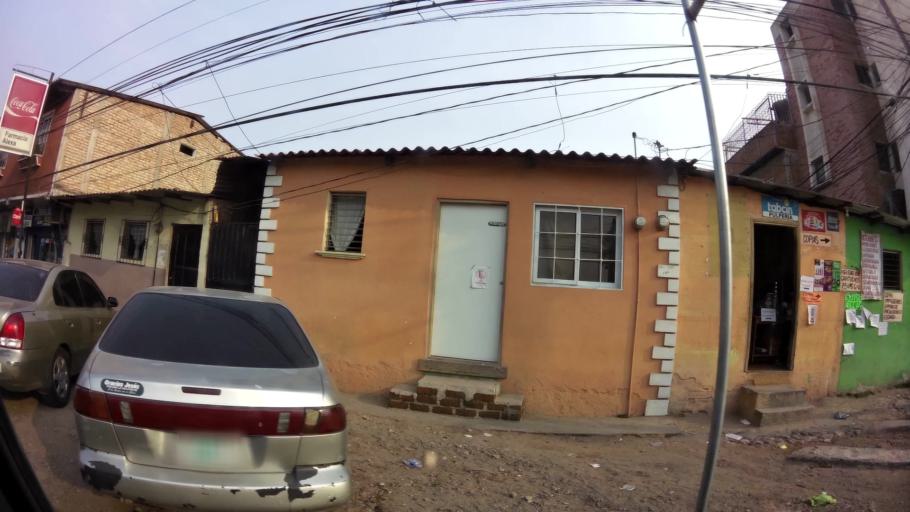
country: HN
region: Francisco Morazan
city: Tegucigalpa
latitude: 14.0680
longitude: -87.1831
